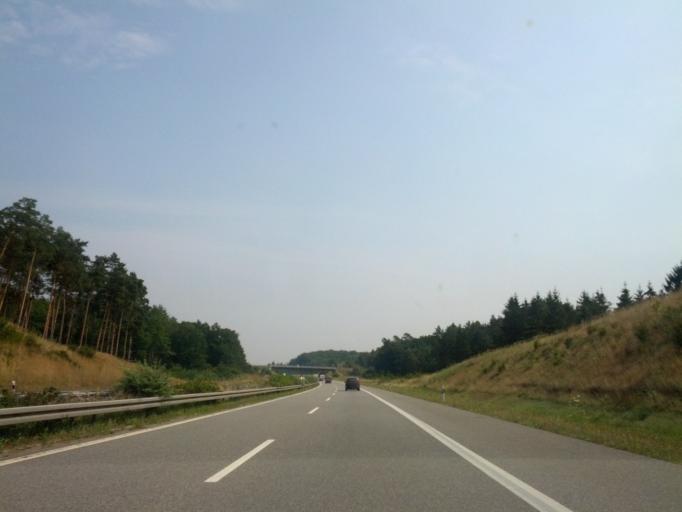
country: DE
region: Mecklenburg-Vorpommern
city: Tessin
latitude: 54.0107
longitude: 12.4612
